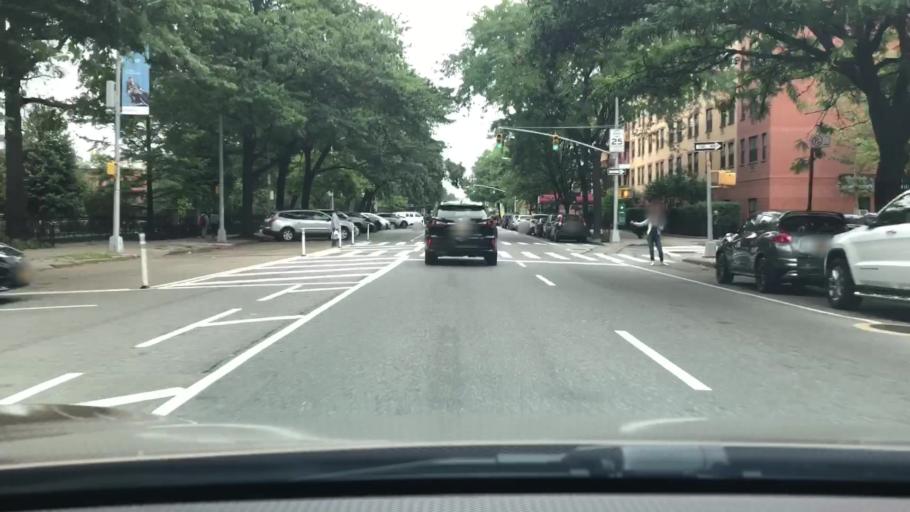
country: US
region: New York
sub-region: New York County
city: Manhattan
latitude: 40.8036
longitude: -73.9423
